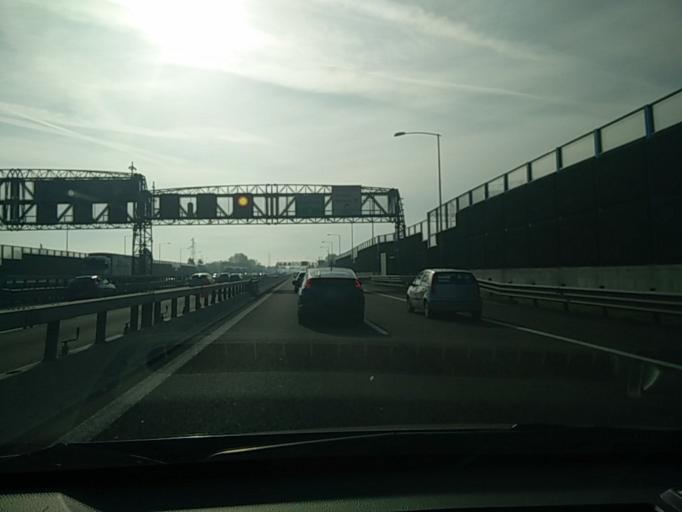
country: IT
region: Emilia-Romagna
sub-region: Provincia di Bologna
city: San Lazzaro
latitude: 44.4878
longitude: 11.4001
